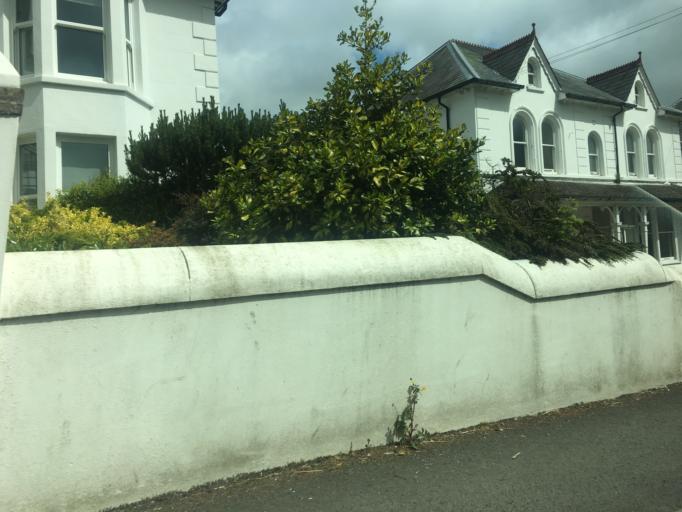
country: GB
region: Wales
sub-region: County of Ceredigion
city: Lampeter
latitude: 52.1162
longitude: -4.0771
